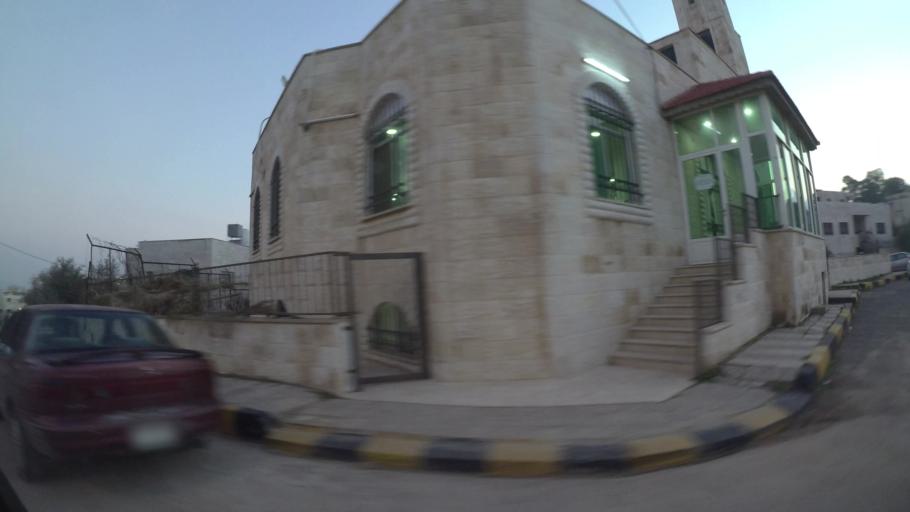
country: JO
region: Amman
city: Al Bunayyat ash Shamaliyah
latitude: 31.8919
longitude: 35.9222
